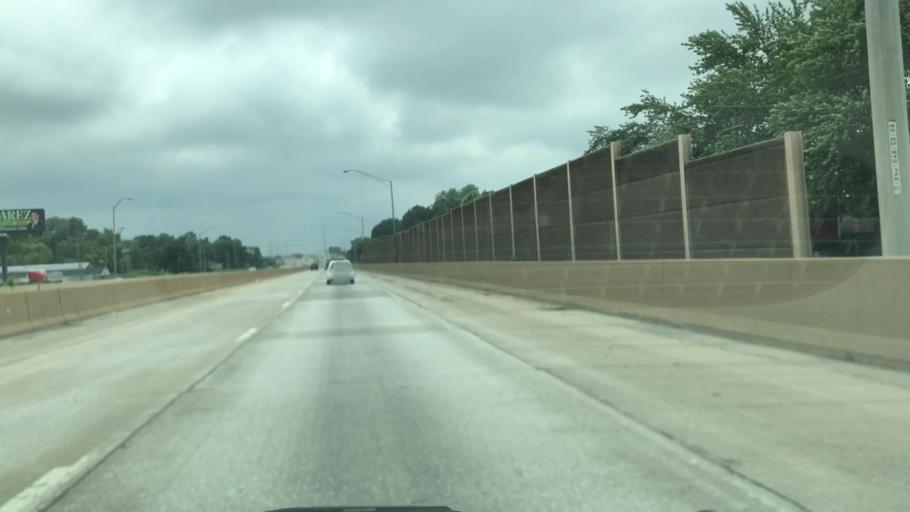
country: US
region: Indiana
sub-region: Lake County
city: Highland
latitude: 41.5837
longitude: -87.4329
